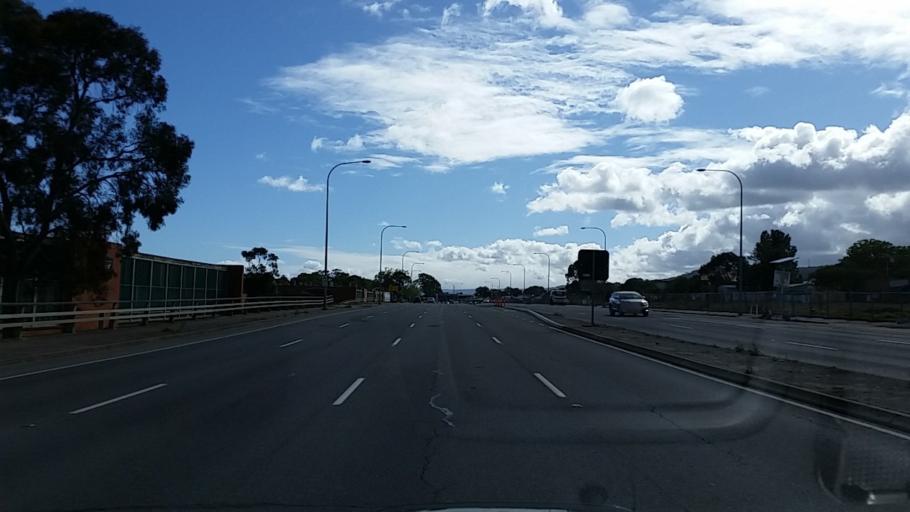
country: AU
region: South Australia
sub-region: Marion
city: Marion
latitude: -35.0145
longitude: 138.5722
